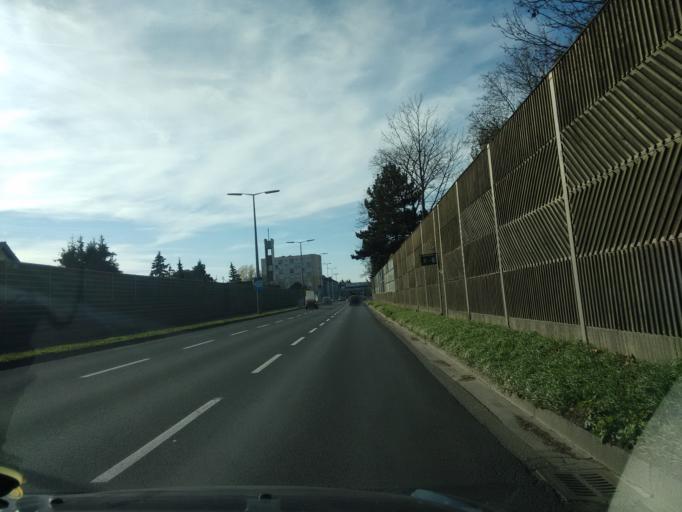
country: AT
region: Upper Austria
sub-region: Politischer Bezirk Linz-Land
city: Leonding
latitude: 48.2571
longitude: 14.2905
